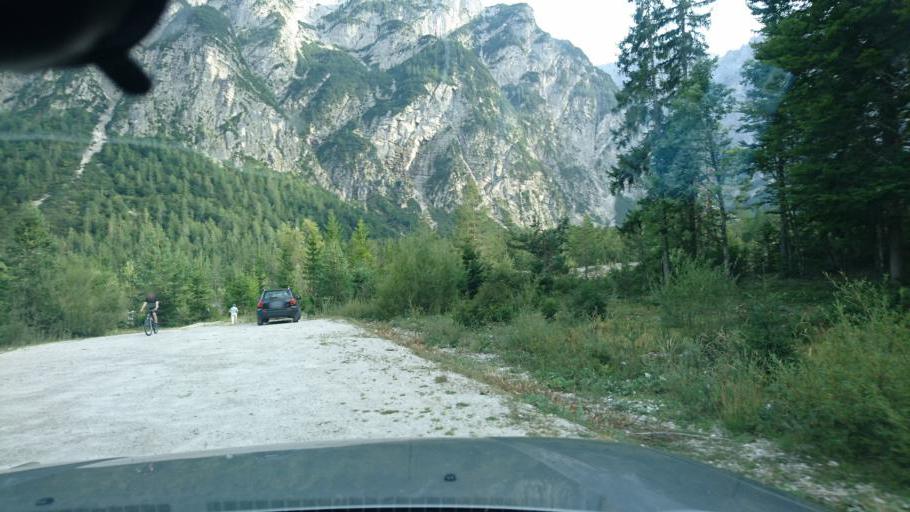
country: IT
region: Friuli Venezia Giulia
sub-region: Provincia di Udine
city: Malborghetto
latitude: 46.4568
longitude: 13.4755
